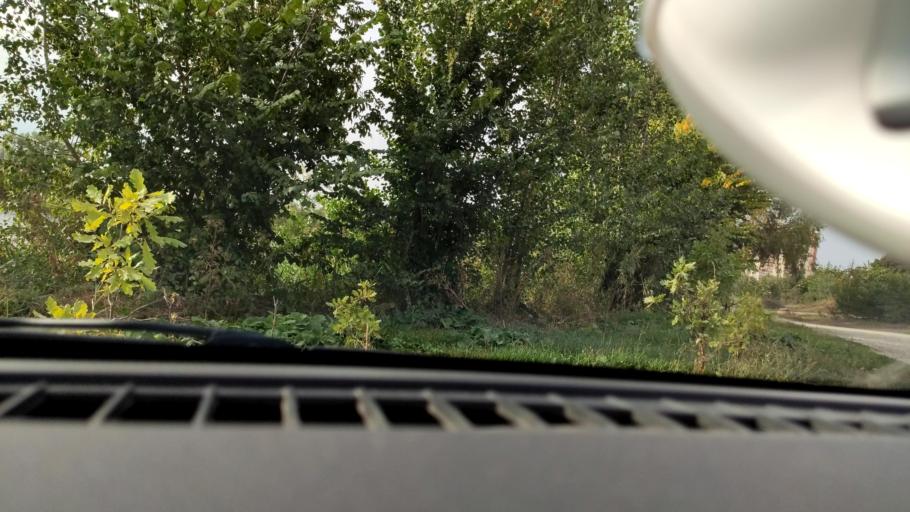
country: RU
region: Samara
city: Samara
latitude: 53.1462
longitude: 50.0882
